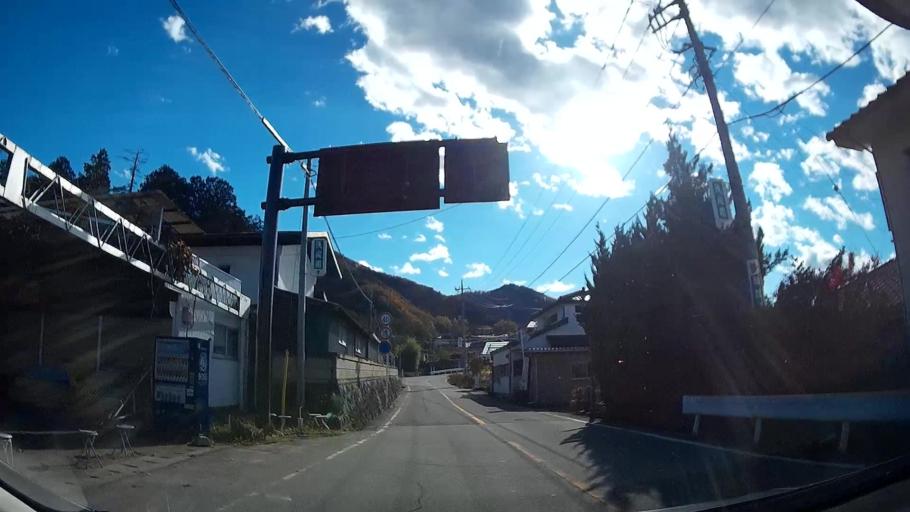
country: JP
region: Yamanashi
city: Enzan
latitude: 35.6512
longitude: 138.7263
